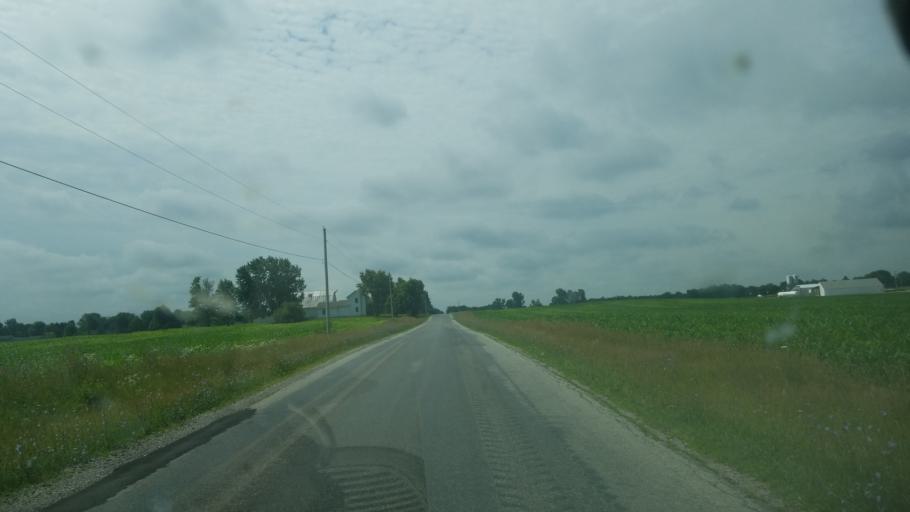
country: US
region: Ohio
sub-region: Licking County
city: Johnstown
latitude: 40.1599
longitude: -82.7593
